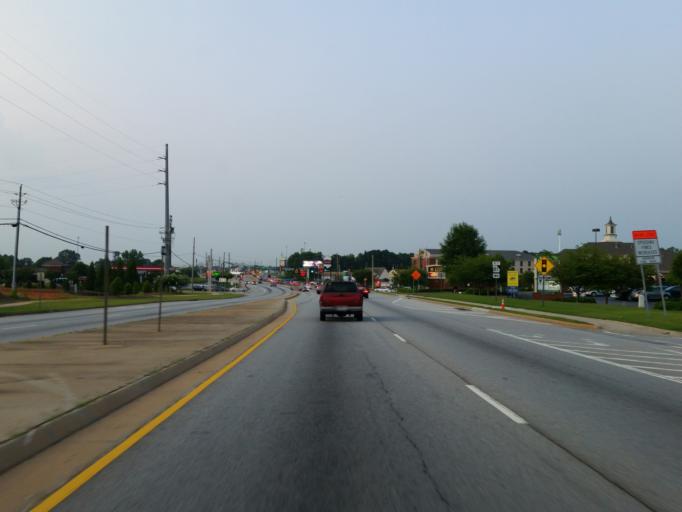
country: US
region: Georgia
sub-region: Henry County
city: McDonough
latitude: 33.4232
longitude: -84.1857
